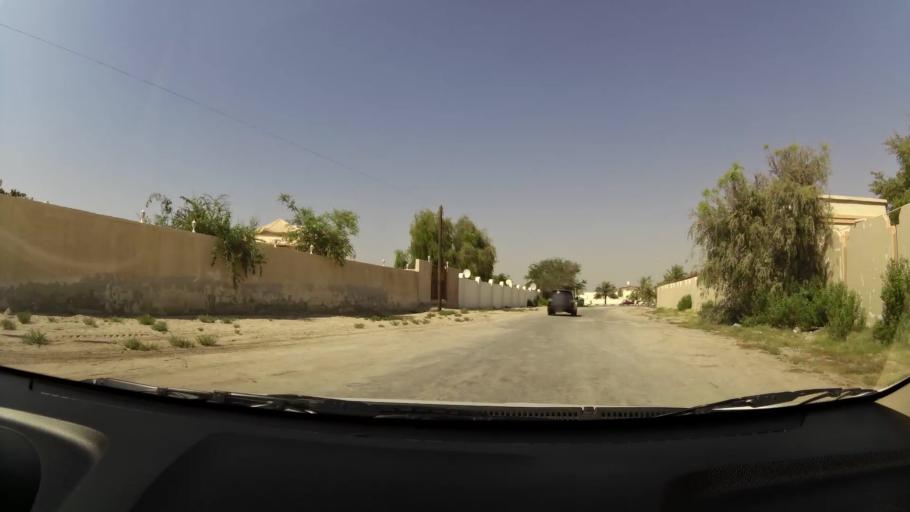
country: AE
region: Ajman
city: Ajman
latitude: 25.4176
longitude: 55.4708
